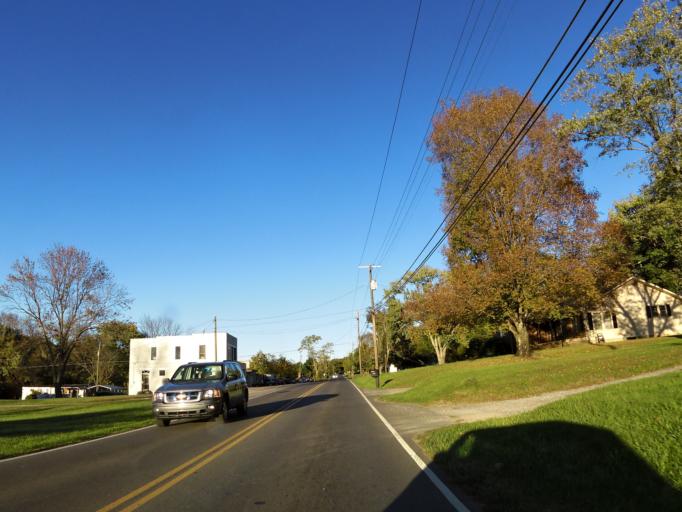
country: US
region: Tennessee
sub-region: Knox County
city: Knoxville
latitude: 35.9931
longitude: -84.0383
